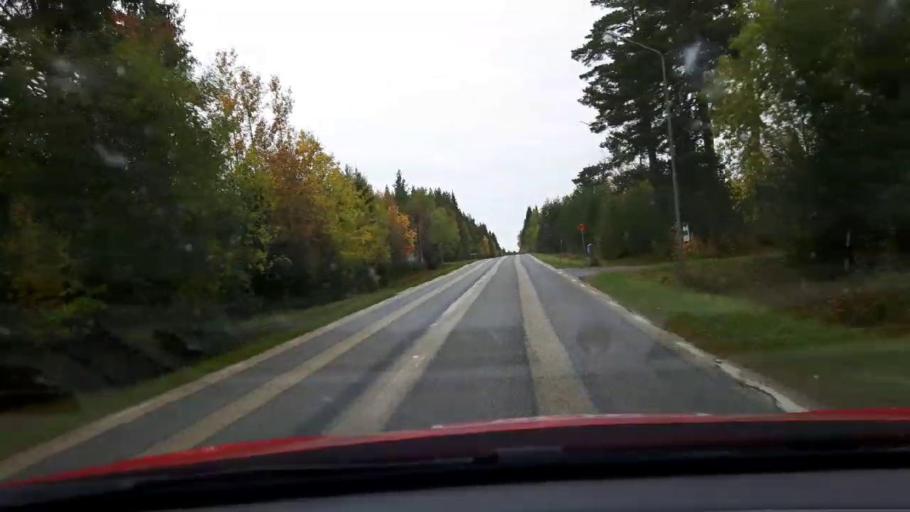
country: SE
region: Jaemtland
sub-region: Bergs Kommun
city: Hoverberg
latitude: 62.8963
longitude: 14.3473
